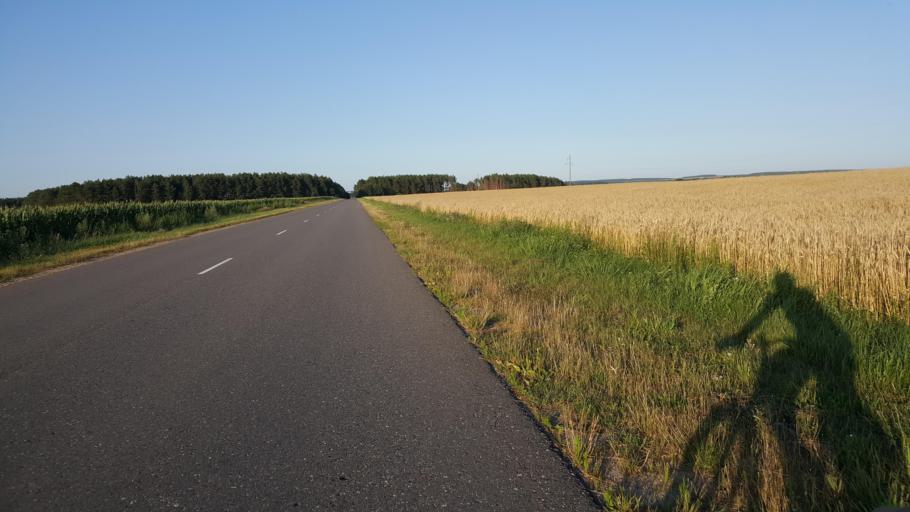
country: BY
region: Brest
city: Kamyanyets
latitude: 52.3873
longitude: 23.7278
